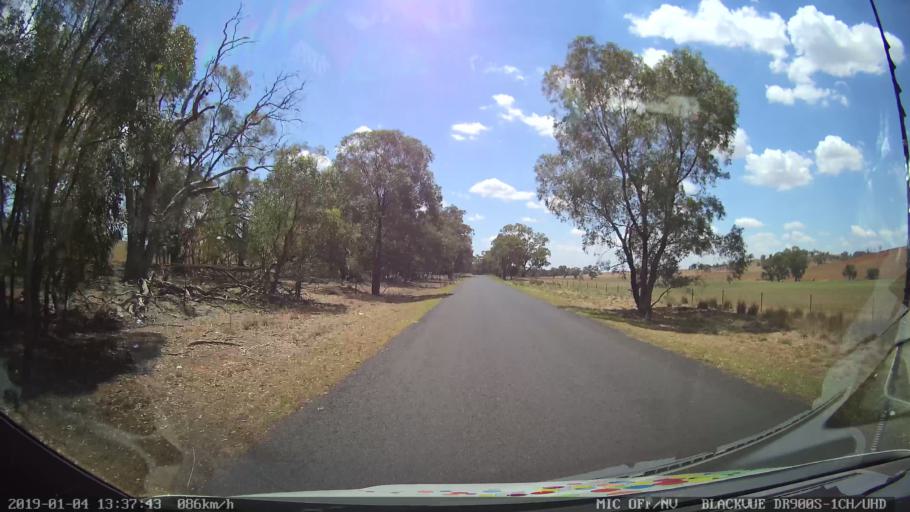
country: AU
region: New South Wales
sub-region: Dubbo Municipality
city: Dubbo
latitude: -32.5467
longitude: 148.5452
